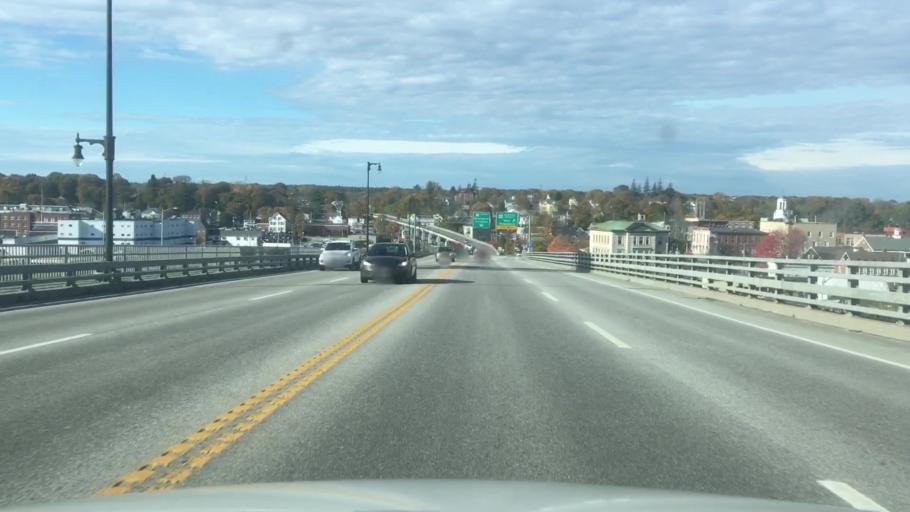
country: US
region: Maine
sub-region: Sagadahoc County
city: Woolwich
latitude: 43.9118
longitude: -69.8095
